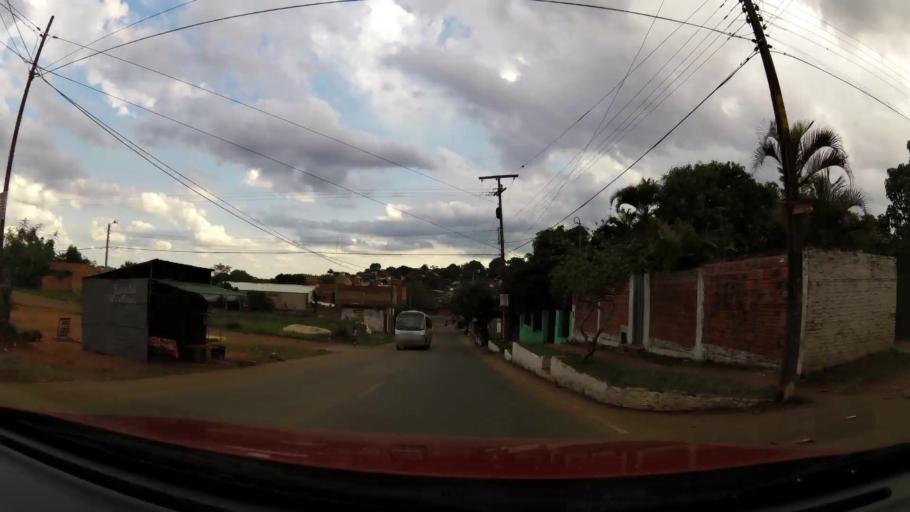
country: PY
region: Central
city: Villa Elisa
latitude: -25.3464
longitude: -57.5612
